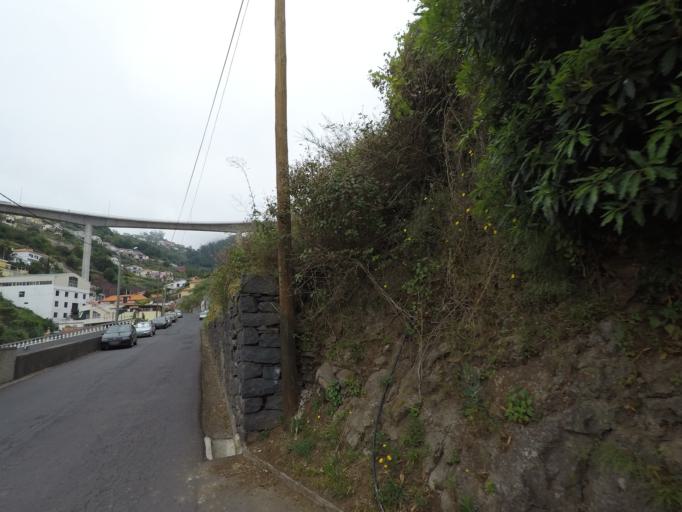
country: PT
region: Madeira
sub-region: Funchal
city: Nossa Senhora do Monte
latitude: 32.6768
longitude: -16.9439
